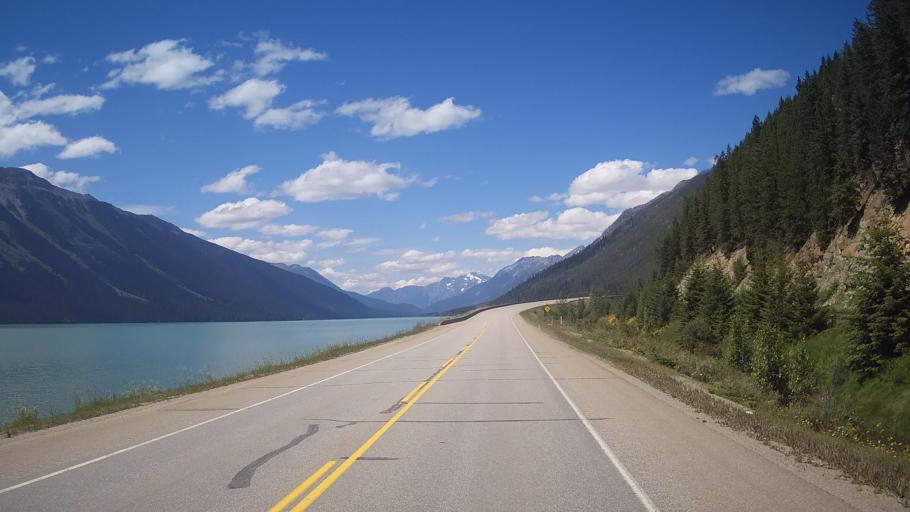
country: CA
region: Alberta
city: Jasper Park Lodge
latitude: 52.9426
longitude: -118.8548
